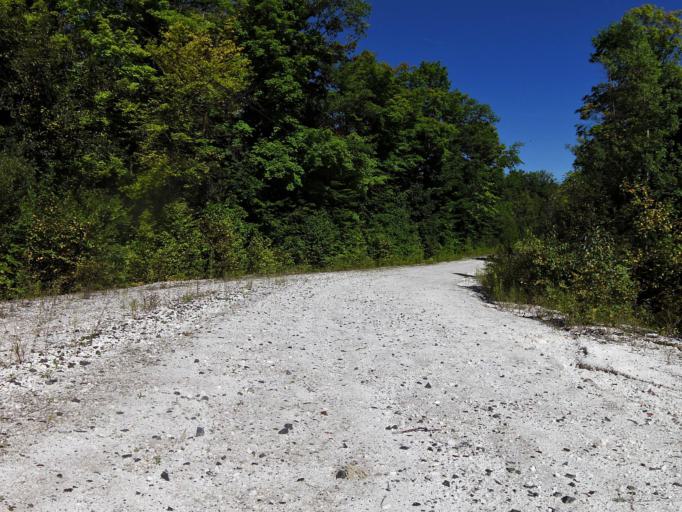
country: CA
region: Ontario
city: Arnprior
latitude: 45.1574
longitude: -76.4956
